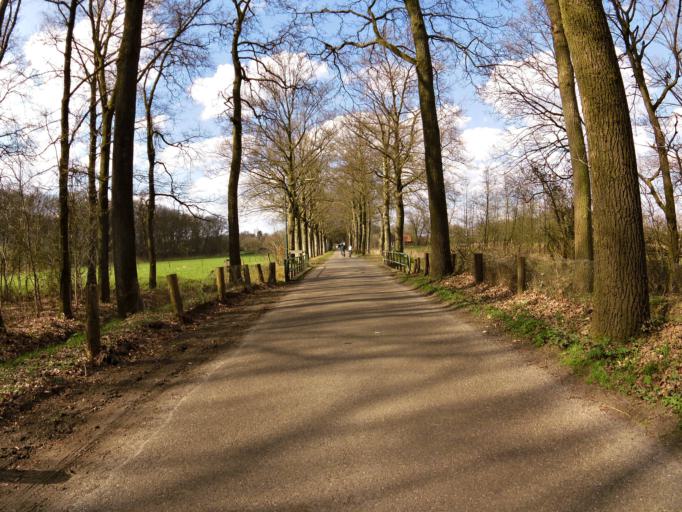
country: NL
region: North Brabant
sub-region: Gemeente Oisterwijk
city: Oisterwijk
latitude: 51.6359
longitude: 5.1709
